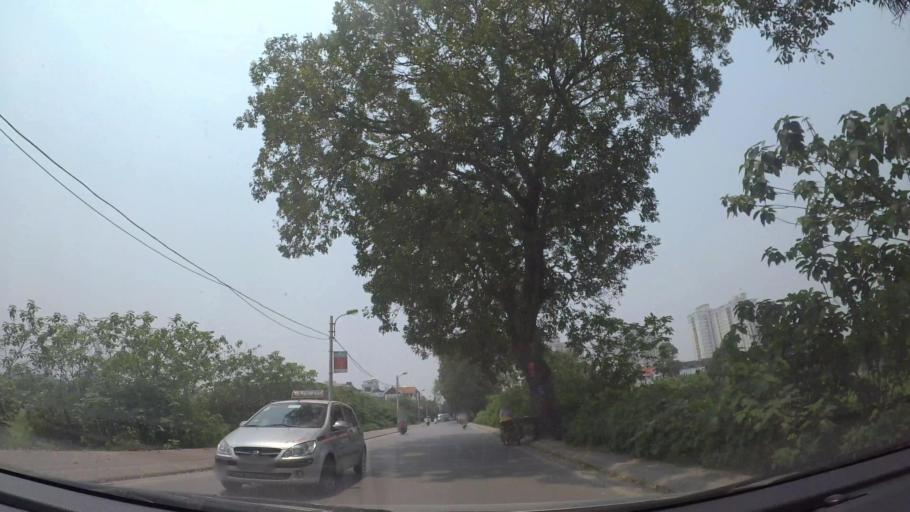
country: VN
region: Ha Noi
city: Thanh Xuan
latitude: 20.9917
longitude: 105.7810
